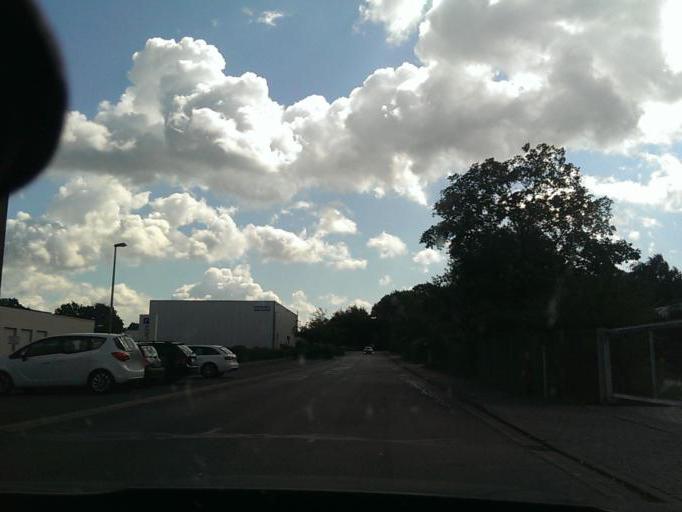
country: DE
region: Lower Saxony
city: Sarstedt
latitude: 52.2486
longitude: 9.8588
